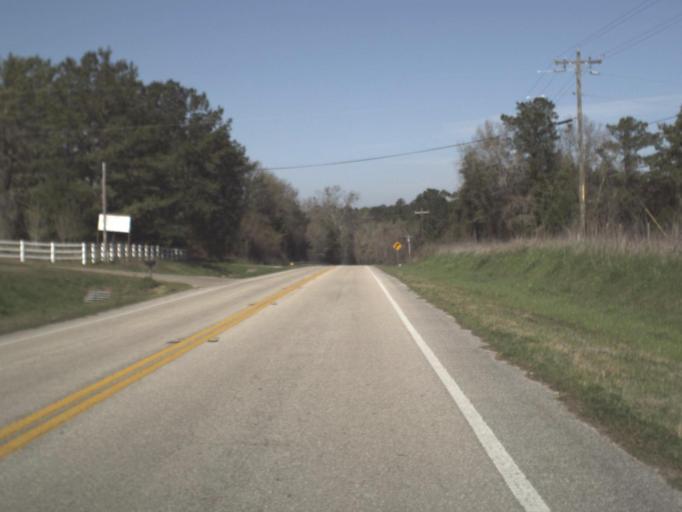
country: US
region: Florida
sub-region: Jefferson County
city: Monticello
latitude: 30.3732
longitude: -83.9978
